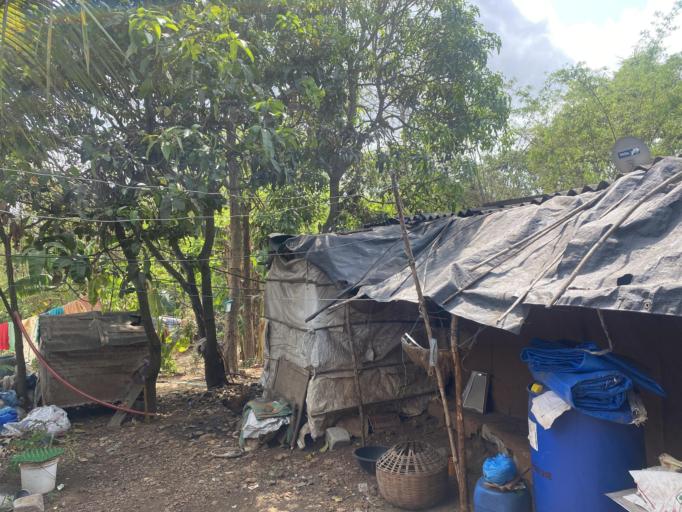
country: IN
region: Gujarat
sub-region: Valsad
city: Vapi
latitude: 20.3186
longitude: 72.8358
